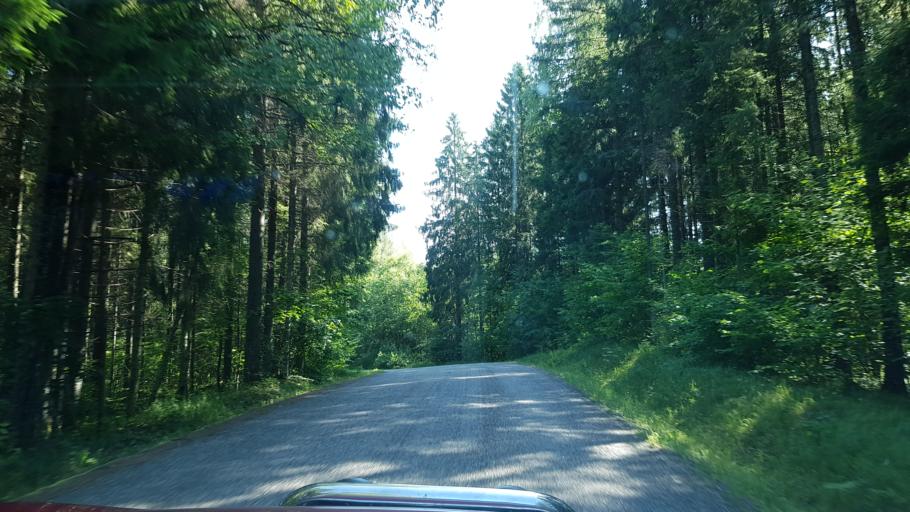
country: EE
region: Vorumaa
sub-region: Voru linn
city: Voru
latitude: 57.7155
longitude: 27.1216
